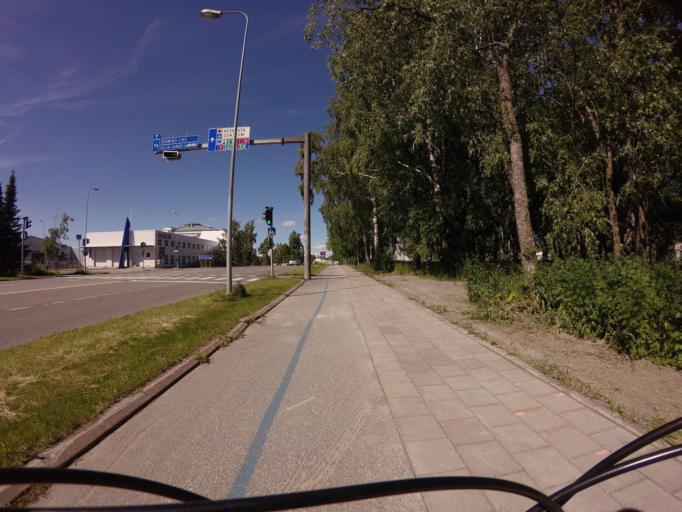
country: FI
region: Varsinais-Suomi
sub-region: Turku
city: Turku
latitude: 60.4379
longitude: 22.2286
